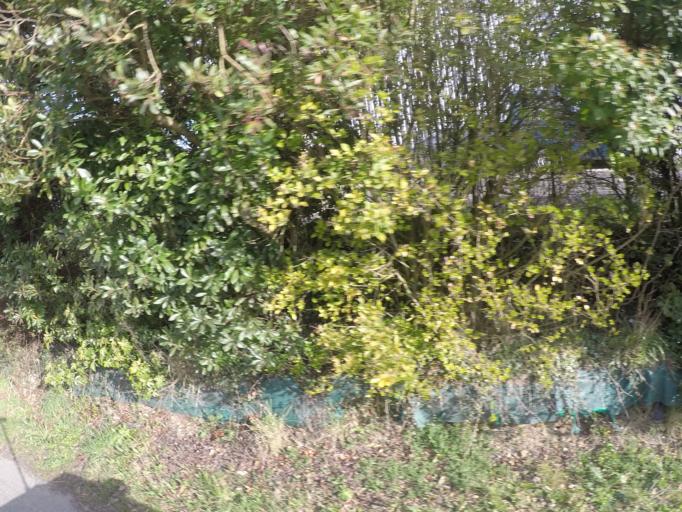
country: FR
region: Brittany
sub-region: Departement des Cotes-d'Armor
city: Plouagat
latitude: 48.5334
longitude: -2.9725
